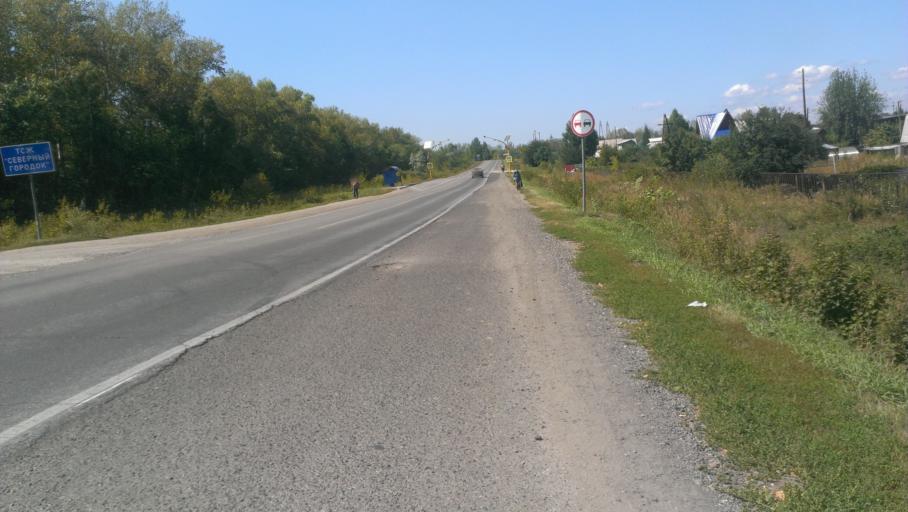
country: RU
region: Altai Krai
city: Nauchnyy Gorodok
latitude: 53.4195
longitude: 83.5444
